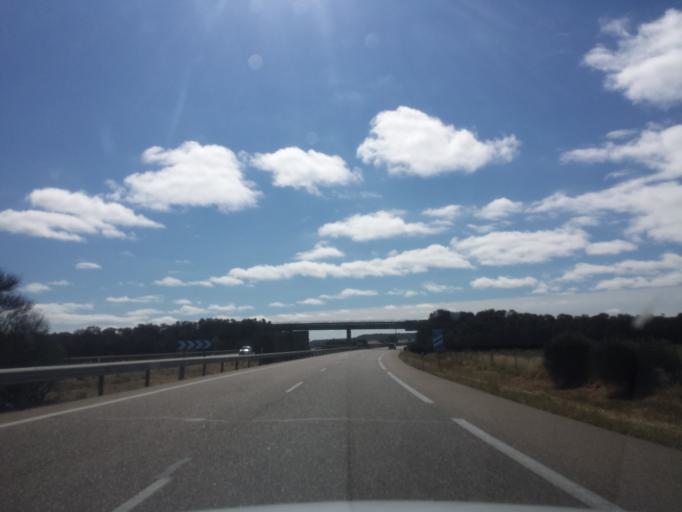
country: ES
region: Castille and Leon
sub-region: Provincia de Valladolid
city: Villardefrades
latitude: 41.7307
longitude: -5.2560
